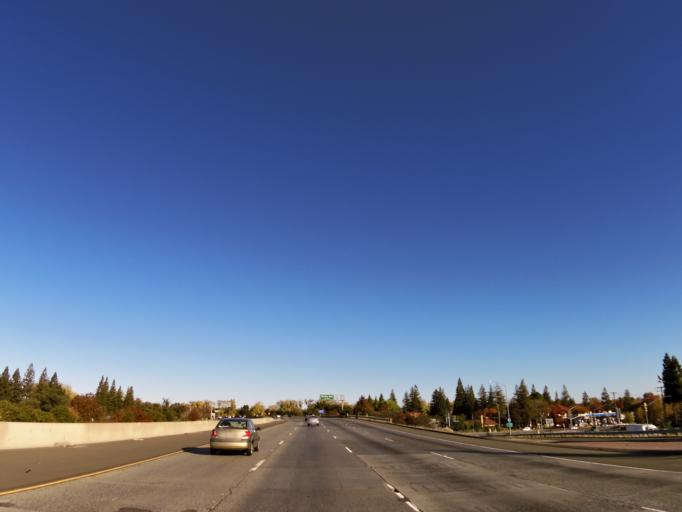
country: US
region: California
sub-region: Sacramento County
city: Sacramento
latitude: 38.5951
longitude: -121.5039
